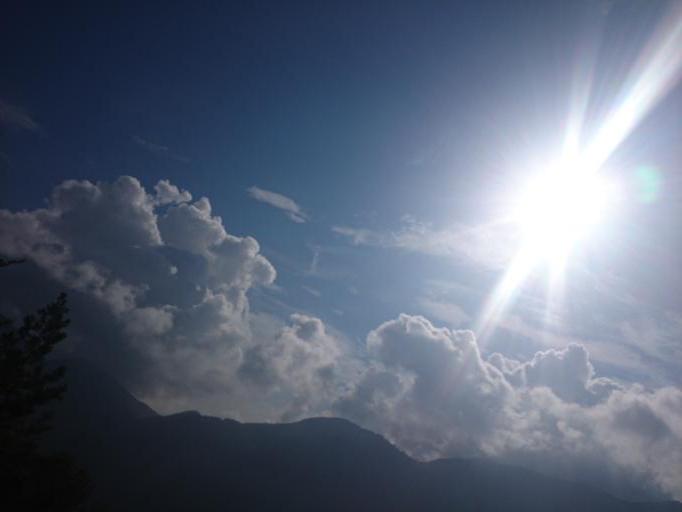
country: AL
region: Diber
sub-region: Rrethi i Dibres
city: Fushe-Lure
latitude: 41.7958
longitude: 20.2100
